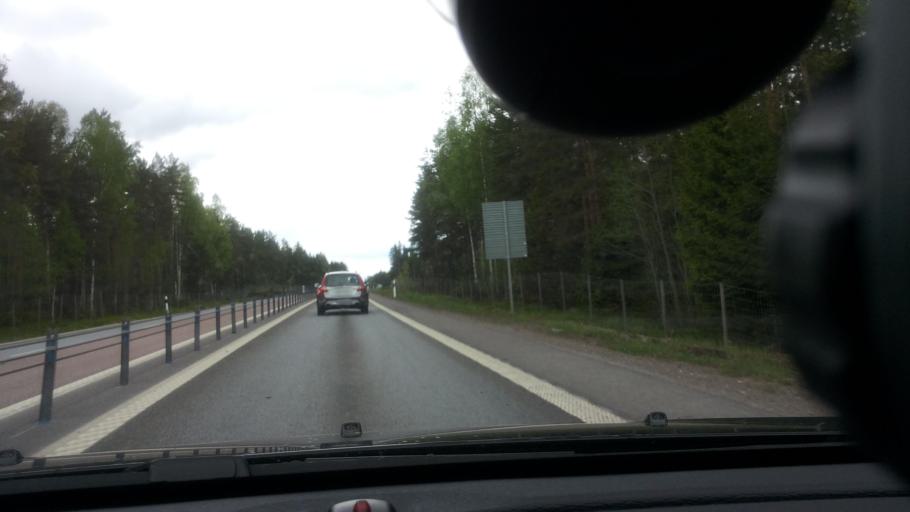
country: SE
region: Gaevleborg
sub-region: Gavle Kommun
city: Norrsundet
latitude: 60.8756
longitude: 17.0482
